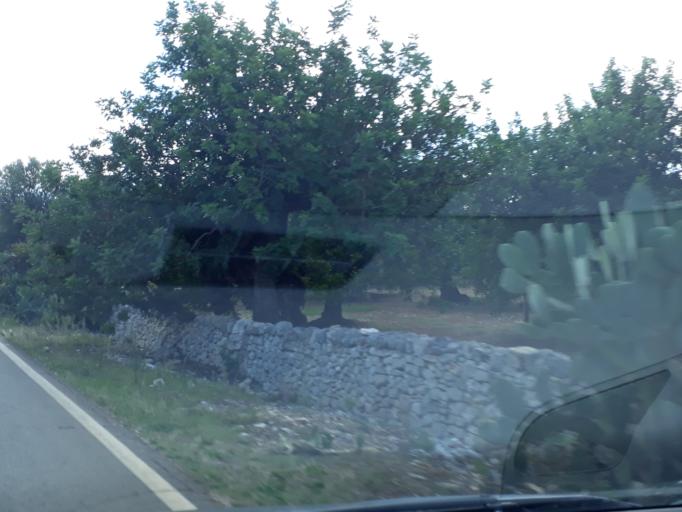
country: IT
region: Apulia
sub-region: Provincia di Brindisi
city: Pezze di Greco
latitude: 40.8120
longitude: 17.3838
